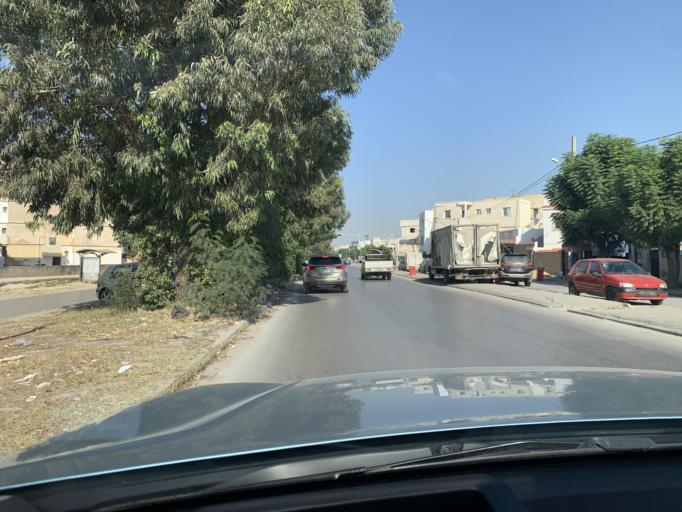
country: TN
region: Manouba
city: Manouba
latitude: 36.8225
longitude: 10.1230
